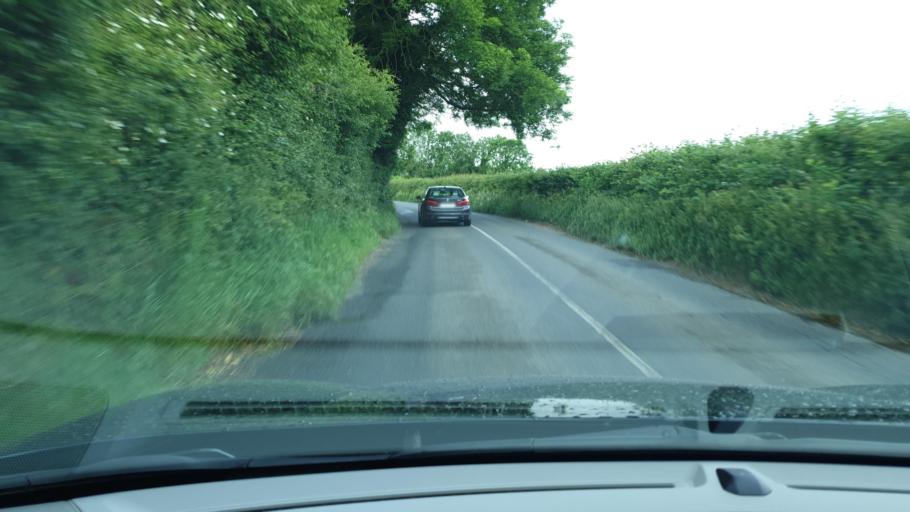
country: IE
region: Leinster
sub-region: An Mhi
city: Ashbourne
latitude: 53.5667
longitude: -6.3648
